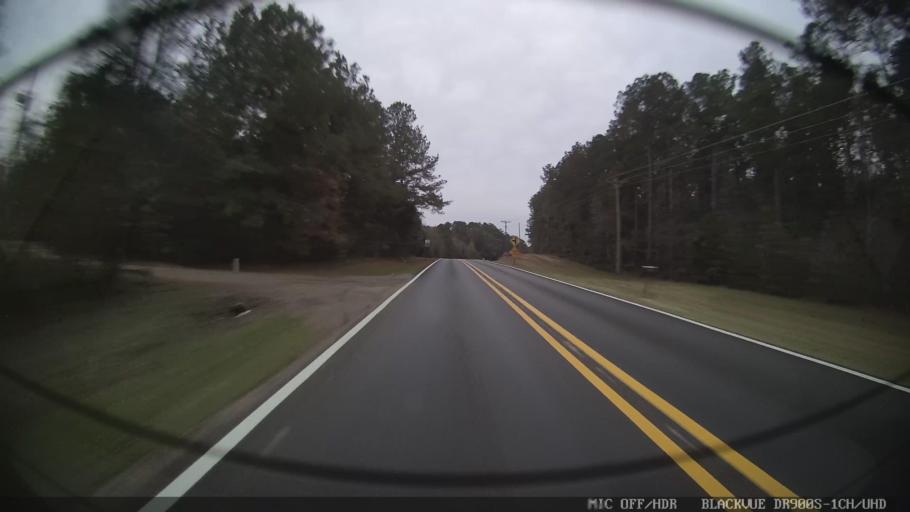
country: US
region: Mississippi
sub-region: Clarke County
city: Quitman
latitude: 32.0470
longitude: -88.6962
